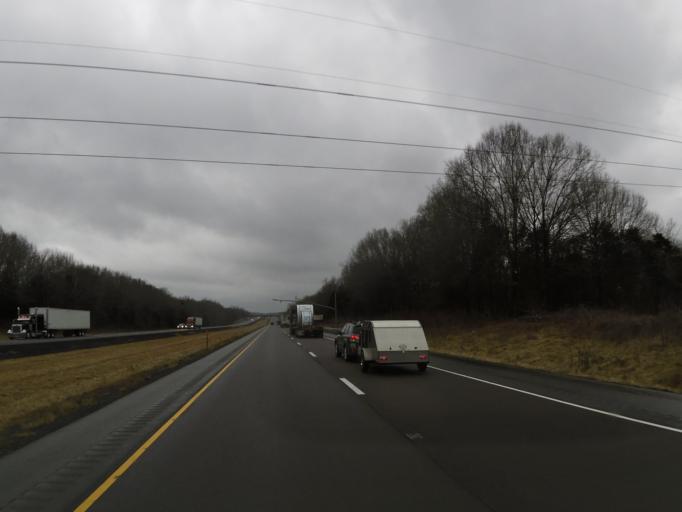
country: US
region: Illinois
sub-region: Williamson County
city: Marion
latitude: 37.6548
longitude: -88.9744
